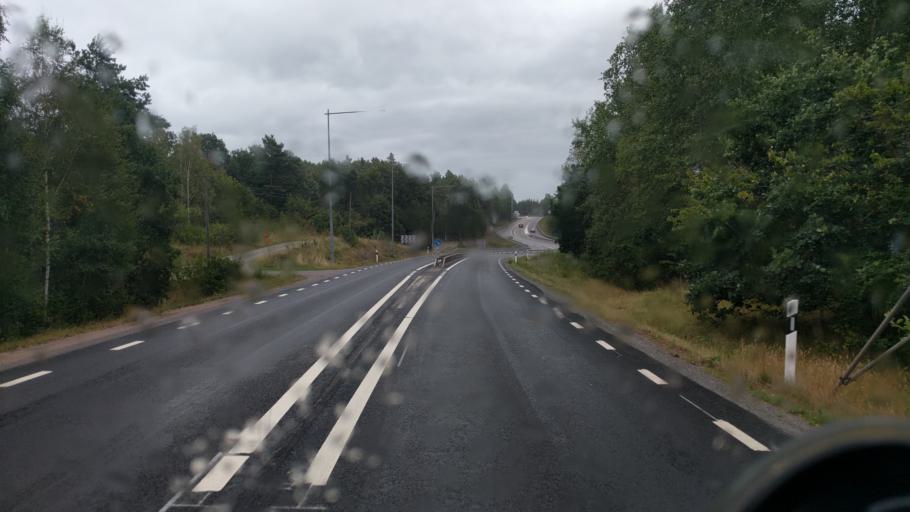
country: SE
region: Kalmar
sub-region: Vasterviks Kommun
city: Ankarsrum
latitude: 57.7229
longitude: 16.4531
